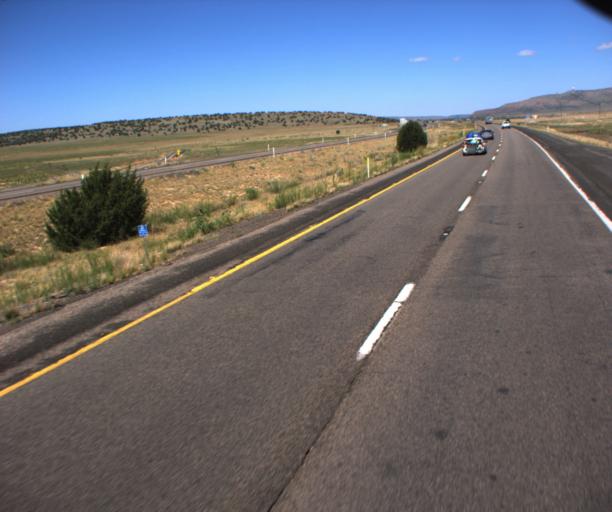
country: US
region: Arizona
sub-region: Yavapai County
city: Paulden
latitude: 35.3141
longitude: -112.8631
